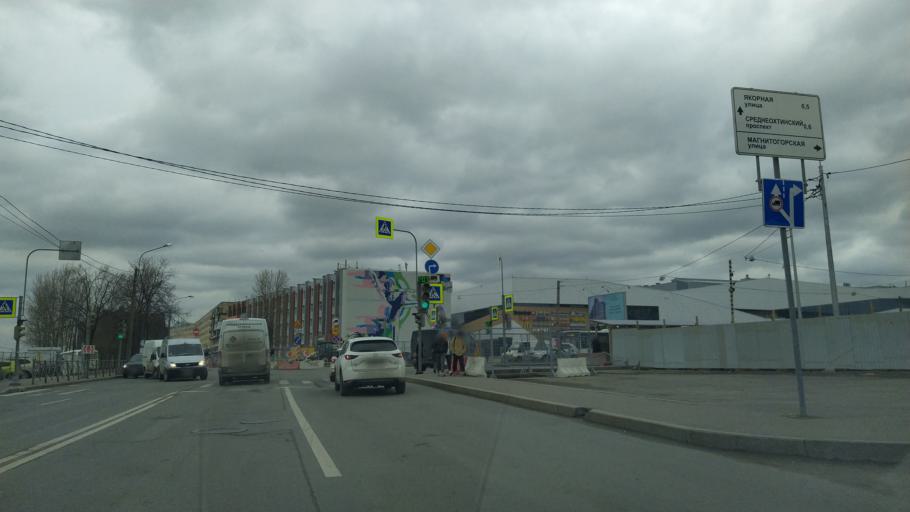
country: RU
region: St.-Petersburg
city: Centralniy
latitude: 59.9374
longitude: 30.4152
